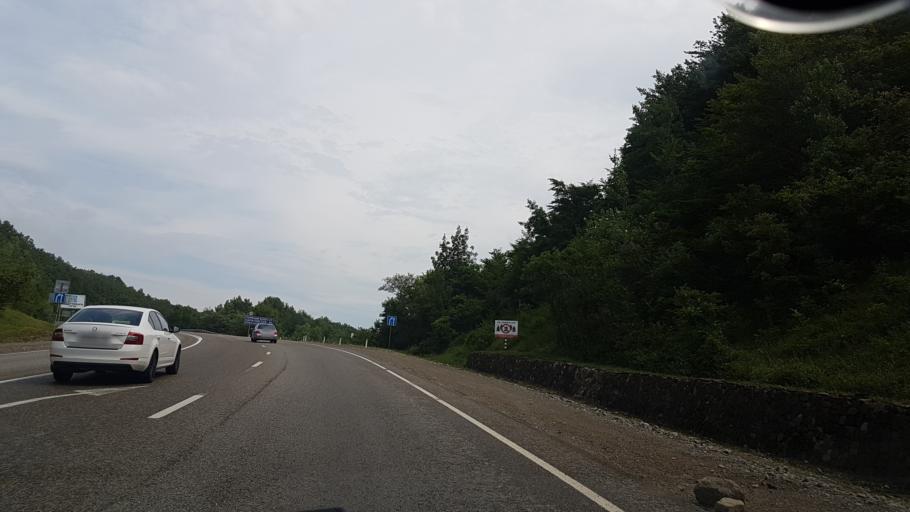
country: RU
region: Krasnodarskiy
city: Novomikhaylovskiy
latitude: 44.4978
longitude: 38.9057
